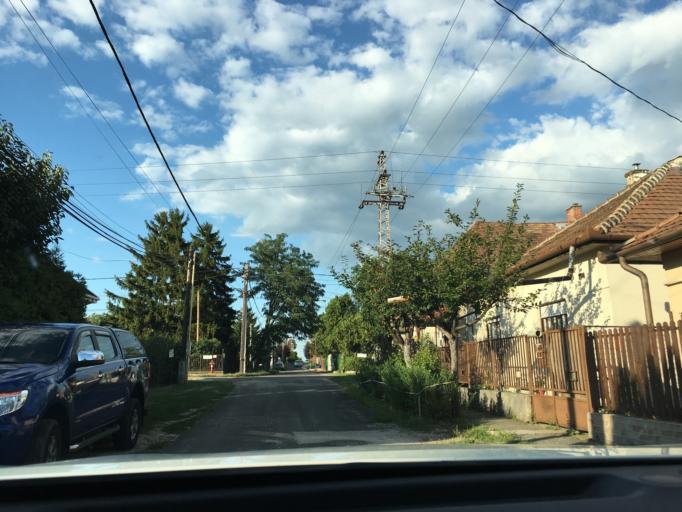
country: HU
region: Budapest
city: Budapest XVII. keruelet
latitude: 47.4694
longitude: 19.2556
